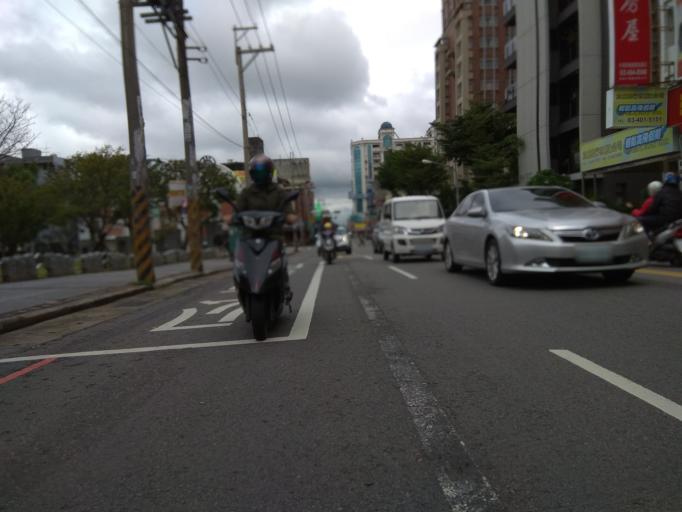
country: TW
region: Taiwan
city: Taoyuan City
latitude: 24.9641
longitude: 121.2172
